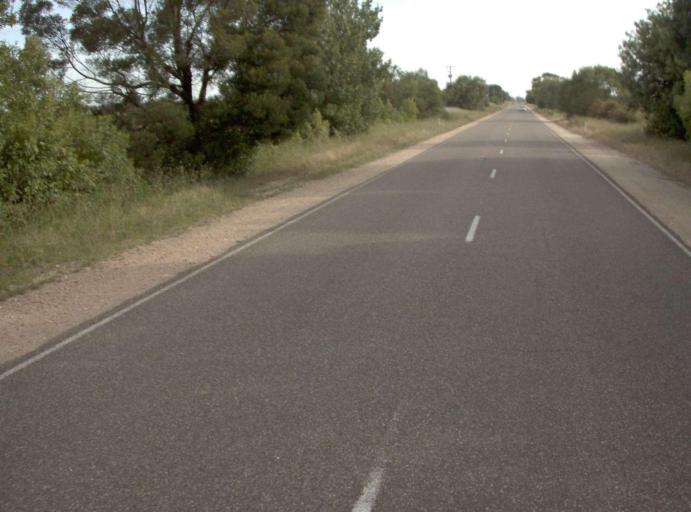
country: AU
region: Victoria
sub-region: Wellington
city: Heyfield
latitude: -37.9771
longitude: 146.8889
